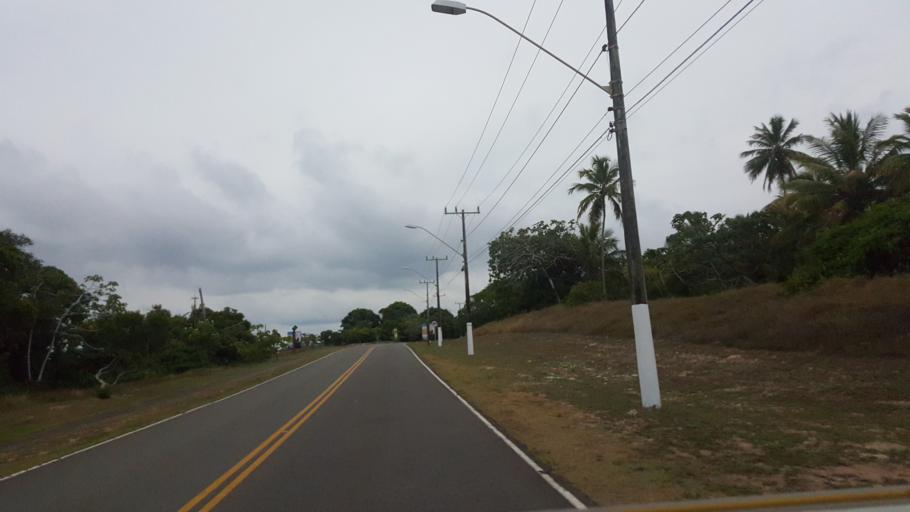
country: BR
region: Bahia
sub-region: Mata De Sao Joao
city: Mata de Sao Joao
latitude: -12.4281
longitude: -37.9211
